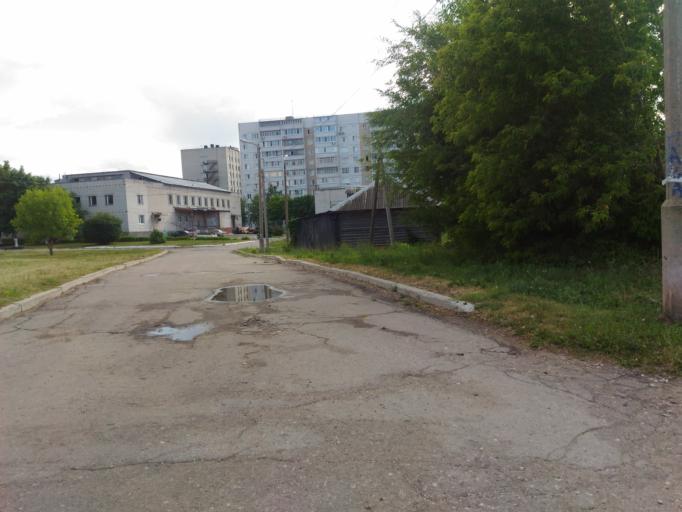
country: RU
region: Ulyanovsk
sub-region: Ulyanovskiy Rayon
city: Ulyanovsk
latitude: 54.3537
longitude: 48.3861
